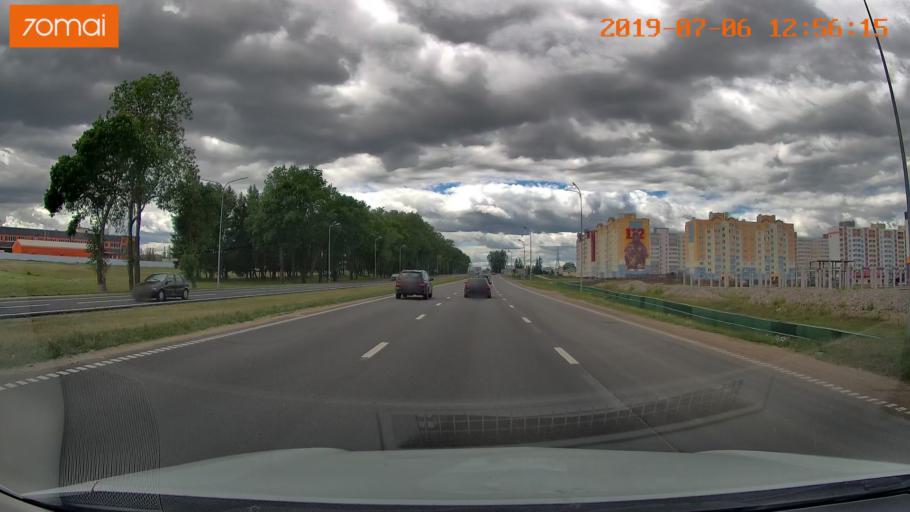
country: BY
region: Minsk
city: Dzyarzhynsk
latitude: 53.6899
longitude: 27.1632
